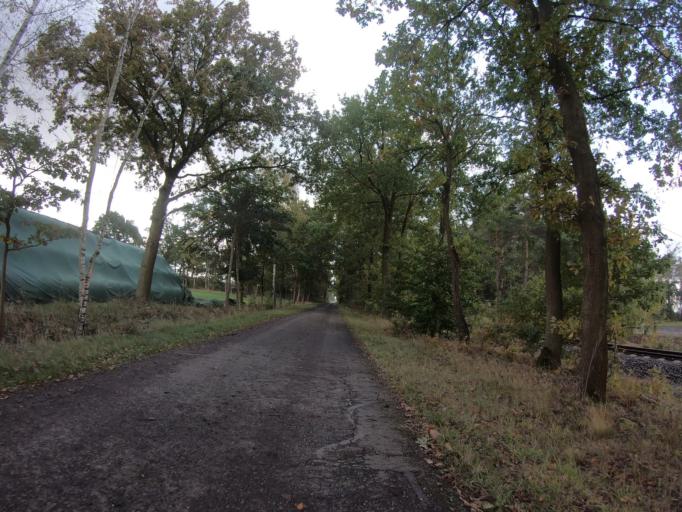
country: DE
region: Lower Saxony
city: Wahrenholz
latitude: 52.5915
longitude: 10.6091
